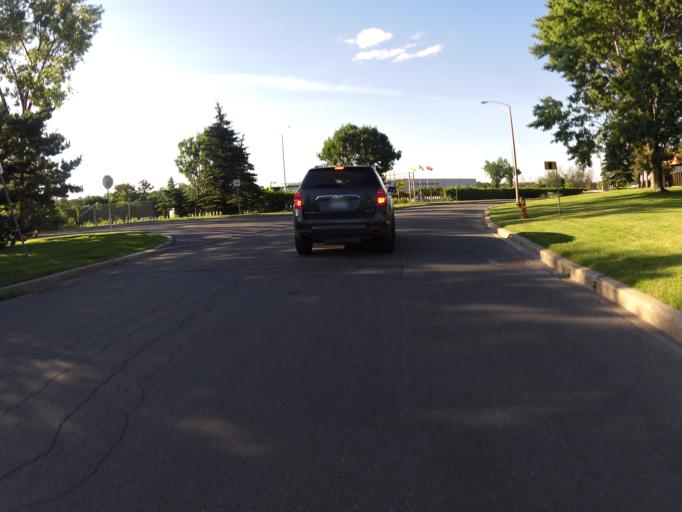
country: CA
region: Ontario
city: Bells Corners
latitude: 45.3523
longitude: -75.7830
